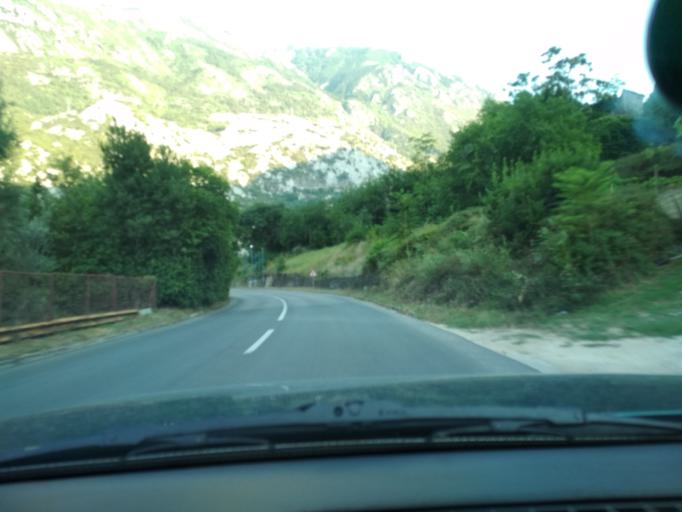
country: ME
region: Kotor
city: Kotor
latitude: 42.4169
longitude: 18.7622
